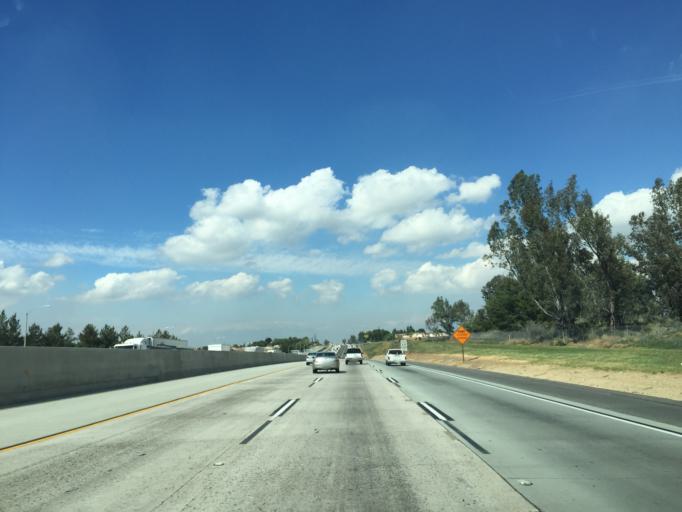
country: US
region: California
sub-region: Riverside County
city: Beaumont
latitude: 33.9503
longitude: -117.0089
